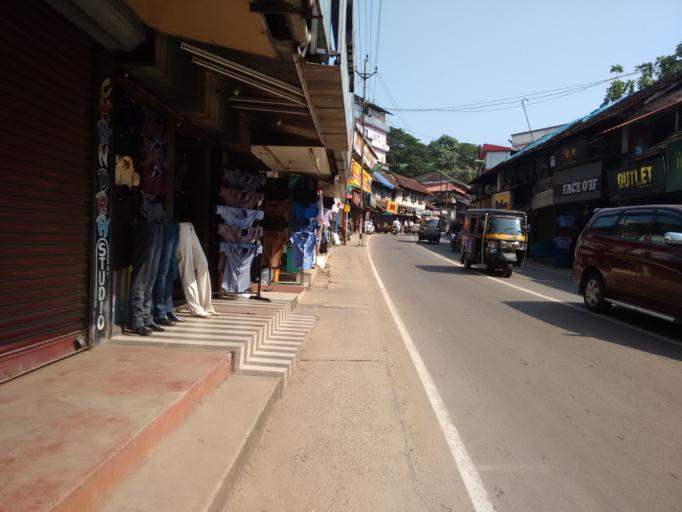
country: IN
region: Kerala
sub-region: Kozhikode
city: Badagara
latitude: 11.5997
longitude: 75.5853
